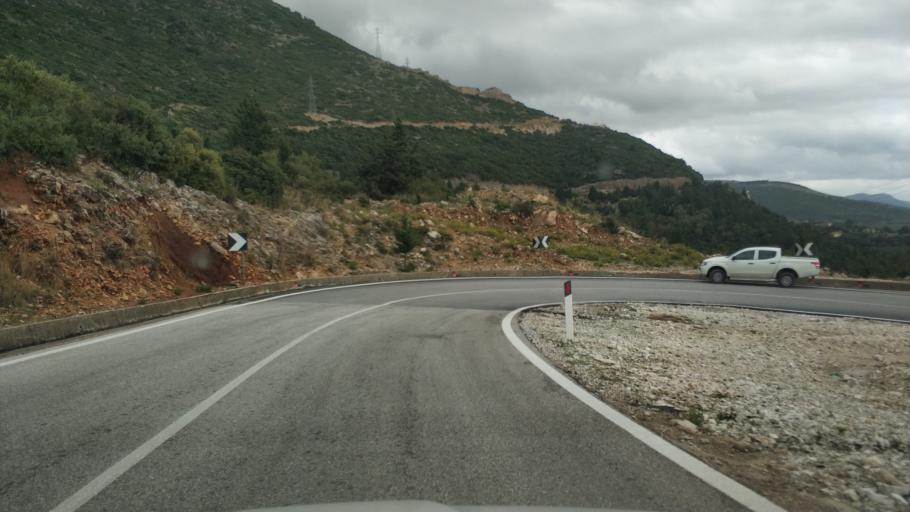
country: AL
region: Vlore
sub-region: Rrethi i Vlores
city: Vranisht
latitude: 40.1437
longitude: 19.6812
